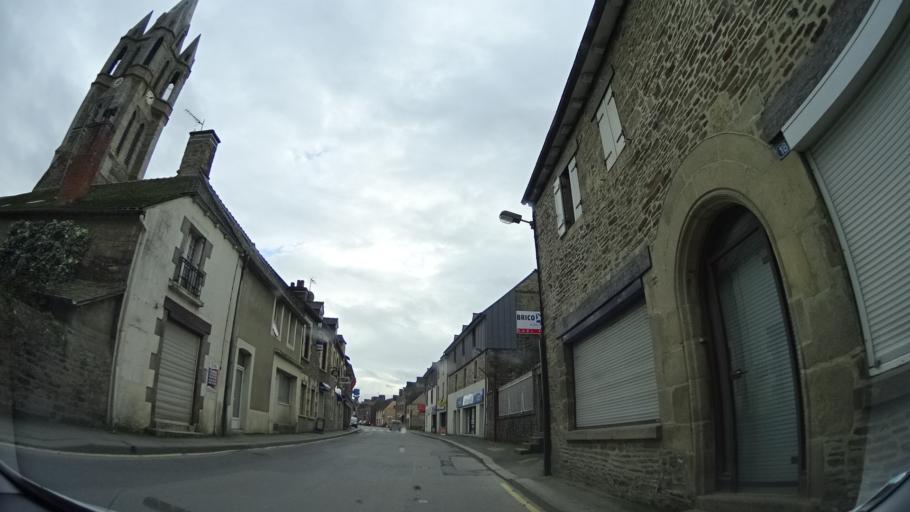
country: FR
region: Brittany
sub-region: Departement des Cotes-d'Armor
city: Evran
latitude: 48.3829
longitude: -1.9809
